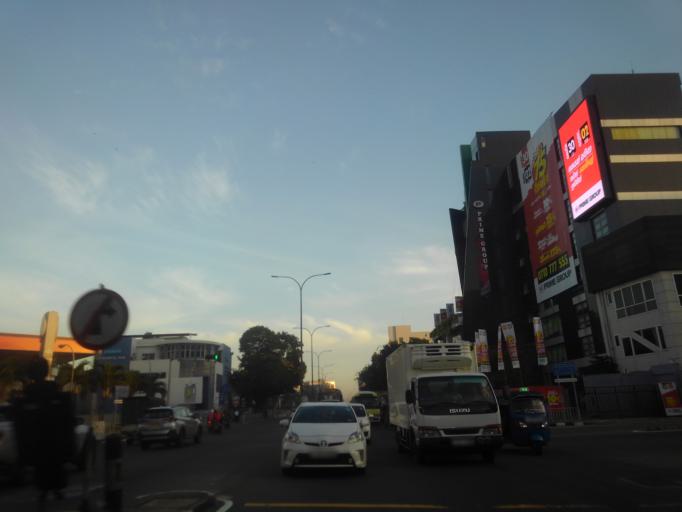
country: LK
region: Western
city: Kolonnawa
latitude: 6.9111
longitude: 79.8775
